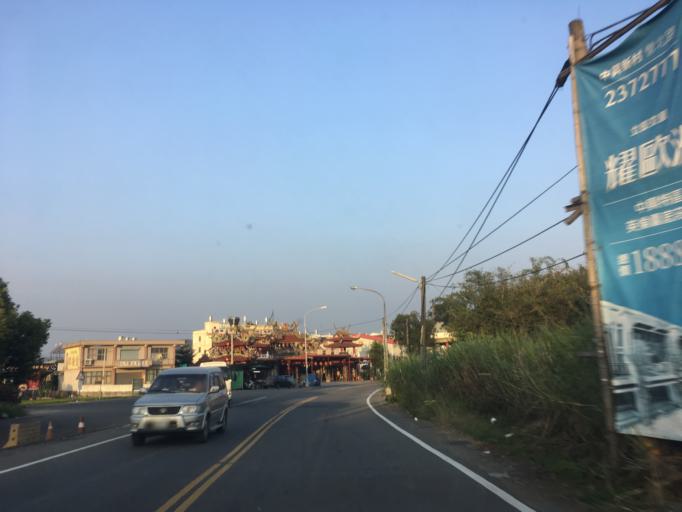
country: TW
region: Taiwan
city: Zhongxing New Village
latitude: 23.9533
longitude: 120.6602
